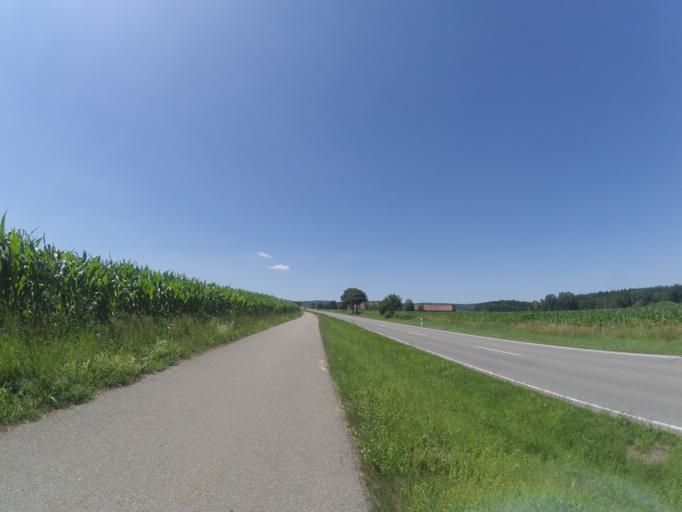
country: DE
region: Baden-Wuerttemberg
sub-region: Tuebingen Region
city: Aulendorf
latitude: 47.9365
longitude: 9.6598
